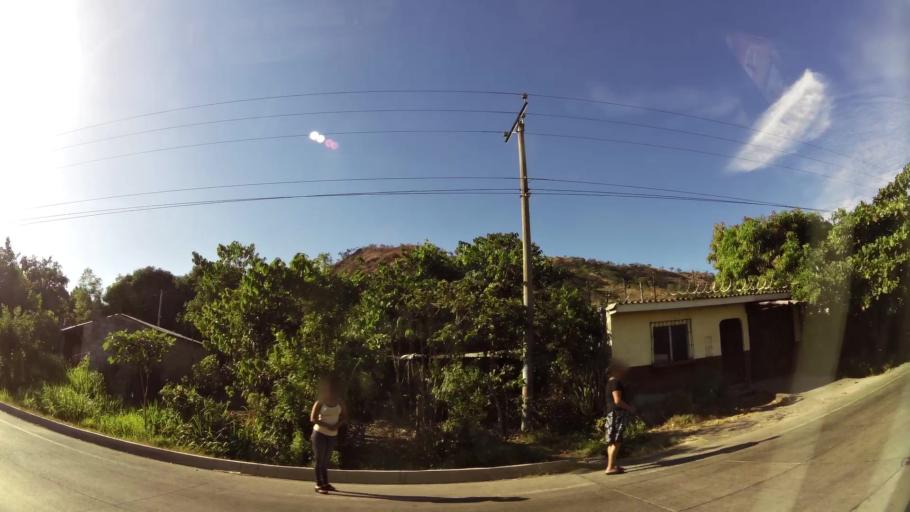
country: SV
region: Santa Ana
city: Santa Ana
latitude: 14.0322
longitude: -89.5252
